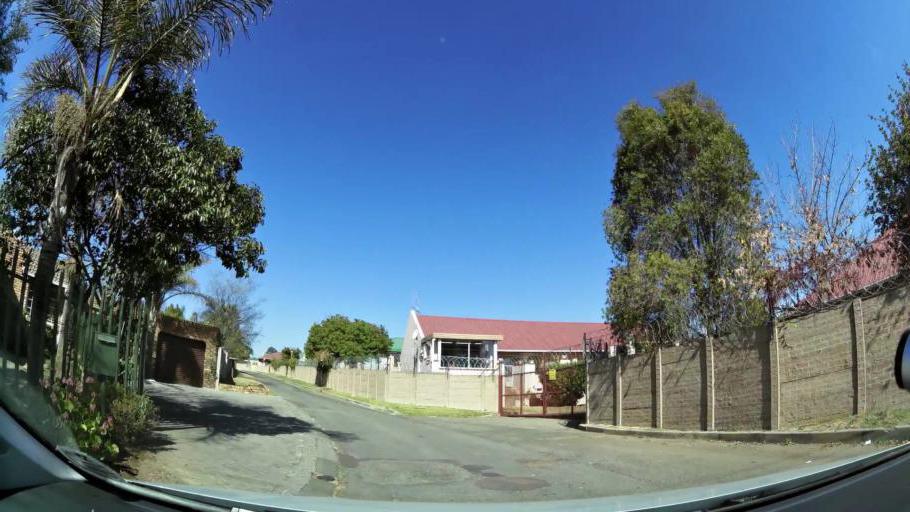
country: ZA
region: Gauteng
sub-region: City of Johannesburg Metropolitan Municipality
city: Modderfontein
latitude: -26.0685
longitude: 28.1965
